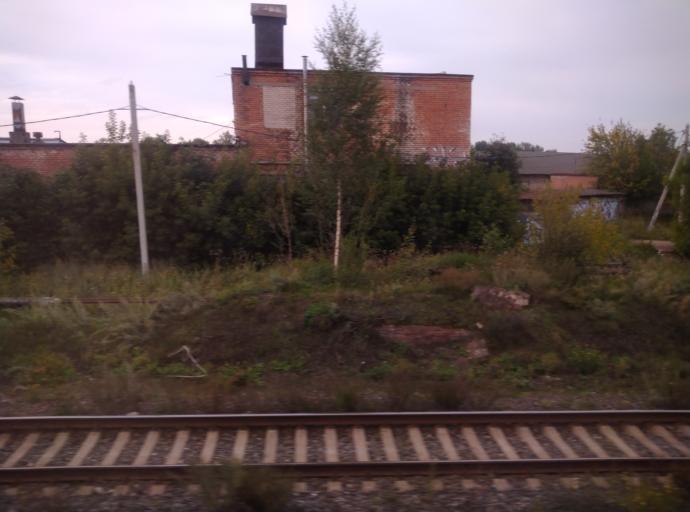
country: RU
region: Jaroslavl
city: Yaroslavl
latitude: 57.6013
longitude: 39.8881
